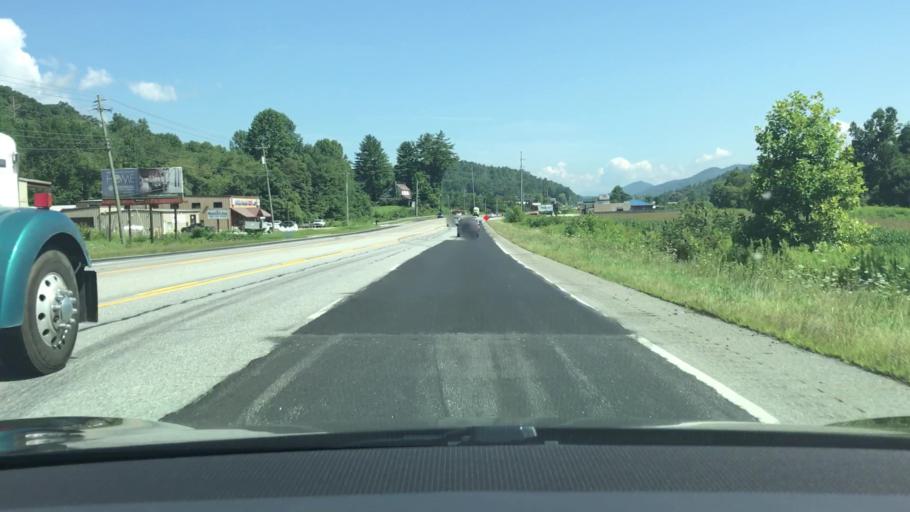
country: US
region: Georgia
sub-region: Rabun County
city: Mountain City
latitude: 34.9320
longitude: -83.3890
